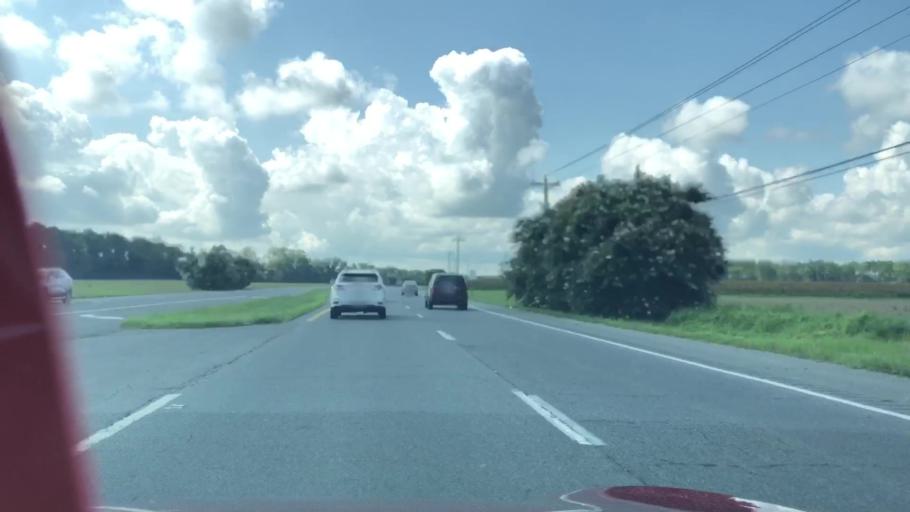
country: US
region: Virginia
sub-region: Accomack County
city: Accomac
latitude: 37.8080
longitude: -75.5945
